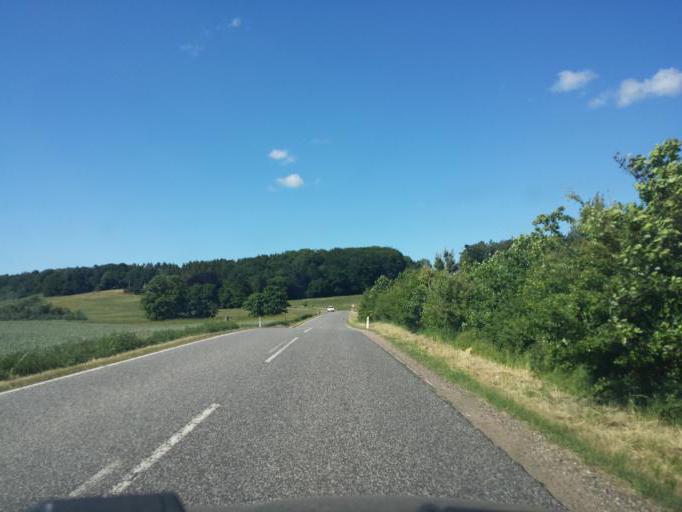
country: DK
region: Capital Region
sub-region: Egedal Kommune
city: Ganlose
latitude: 55.8018
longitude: 12.2643
